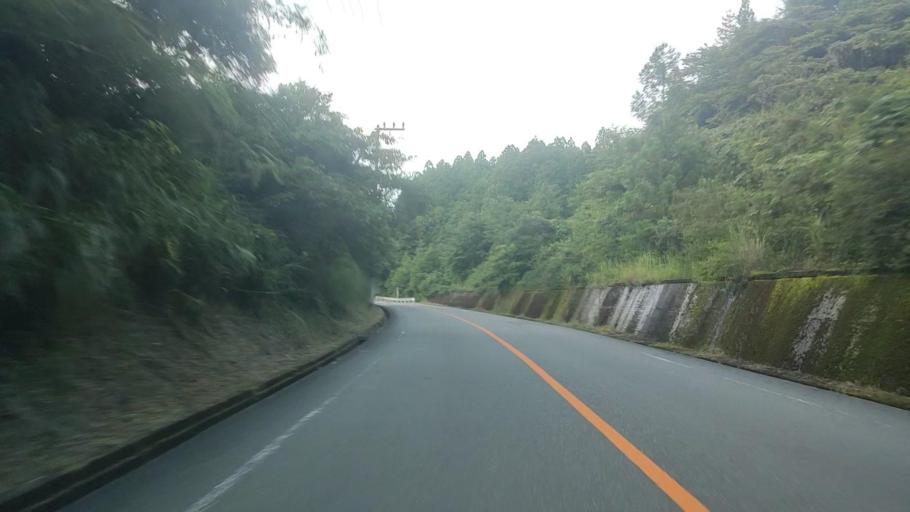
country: JP
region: Wakayama
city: Tanabe
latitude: 33.8176
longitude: 135.6198
